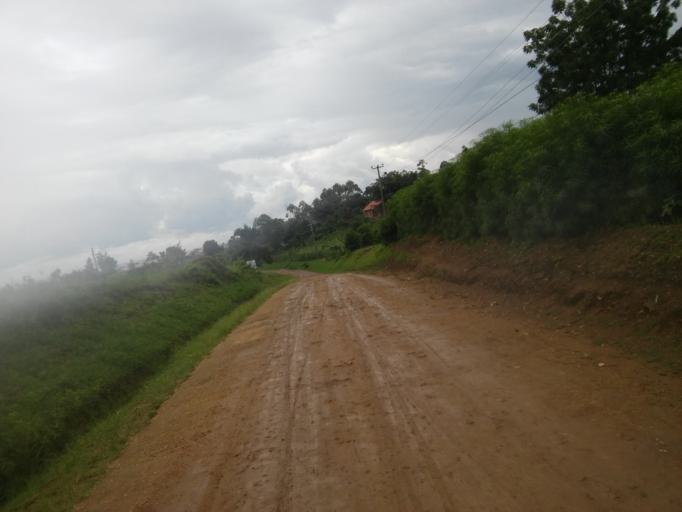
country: UG
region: Eastern Region
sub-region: Mbale District
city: Mbale
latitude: 1.0361
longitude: 34.1950
